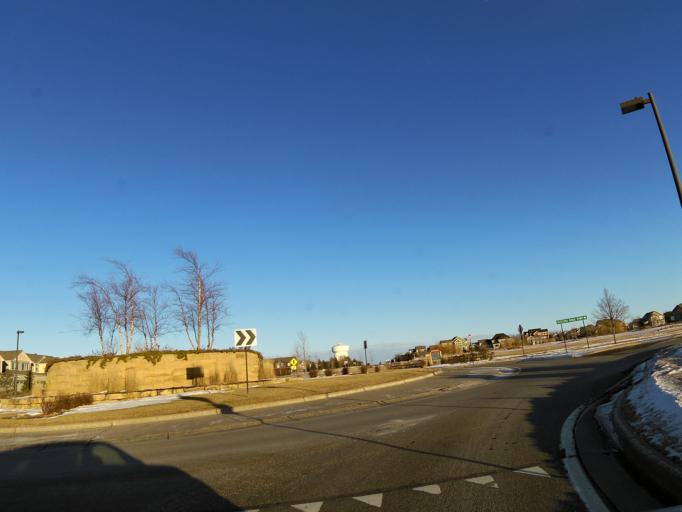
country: US
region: Minnesota
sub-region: Washington County
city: Woodbury
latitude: 44.9019
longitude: -92.8761
